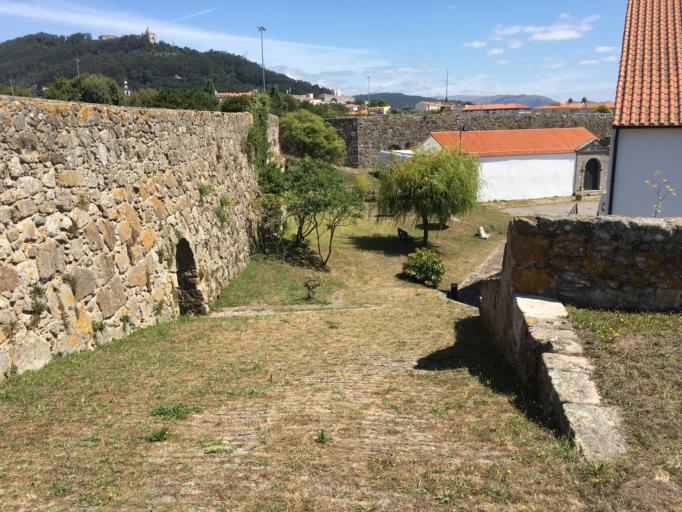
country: PT
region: Viana do Castelo
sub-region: Viana do Castelo
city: Viana do Castelo
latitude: 41.6888
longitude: -8.8390
